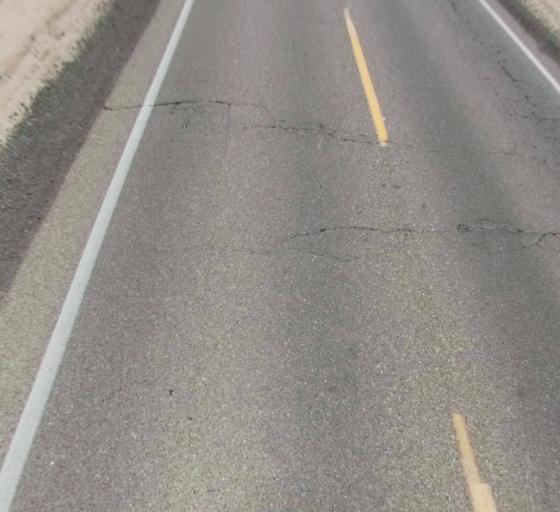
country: US
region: California
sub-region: Fresno County
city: Mendota
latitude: 36.8511
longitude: -120.3014
